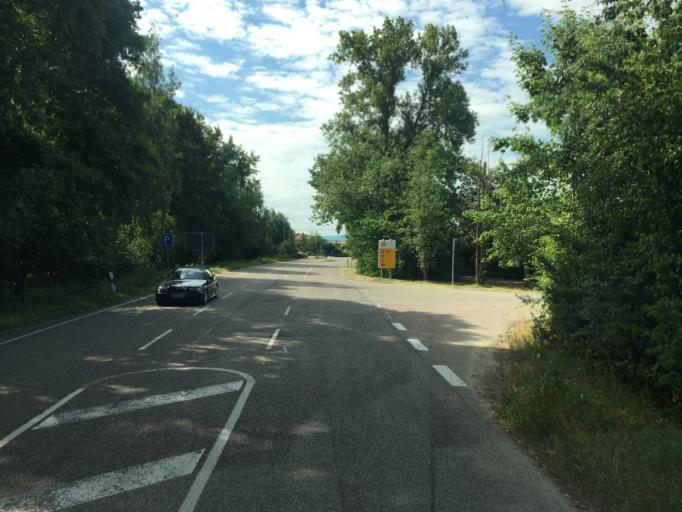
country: DE
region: Baden-Wuerttemberg
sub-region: Freiburg Region
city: Achern
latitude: 48.6431
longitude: 8.0367
